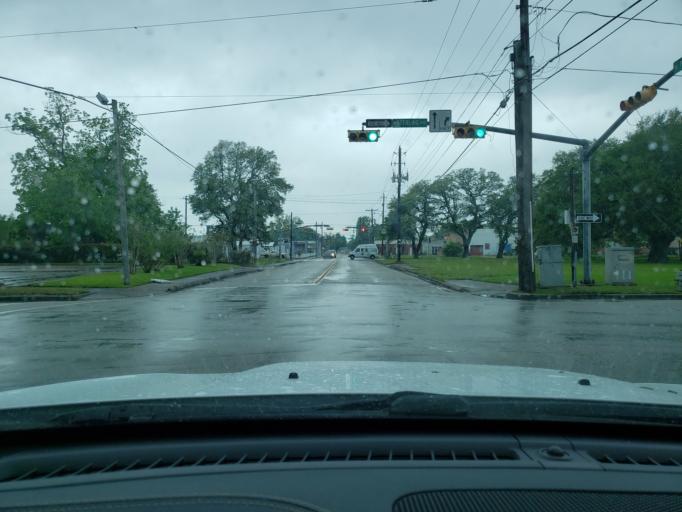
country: US
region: Texas
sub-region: Harris County
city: Baytown
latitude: 29.7352
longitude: -94.9721
